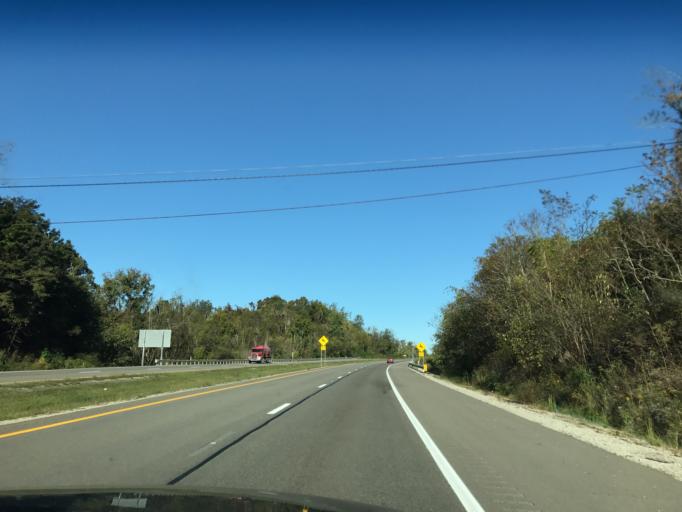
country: US
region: West Virginia
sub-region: Wood County
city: Mineral Wells
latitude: 39.2405
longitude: -81.4663
